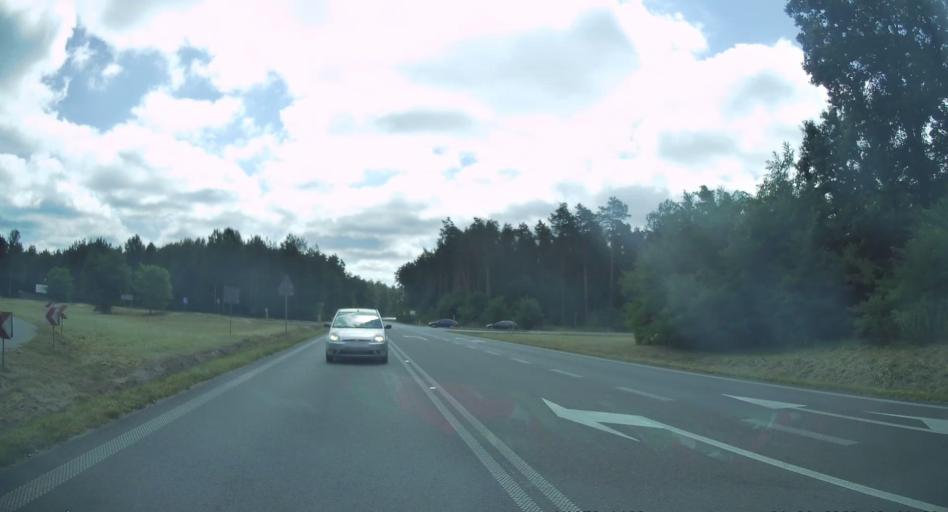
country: PL
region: Subcarpathian Voivodeship
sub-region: Powiat mielecki
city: Mielec
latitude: 50.3164
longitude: 21.5016
